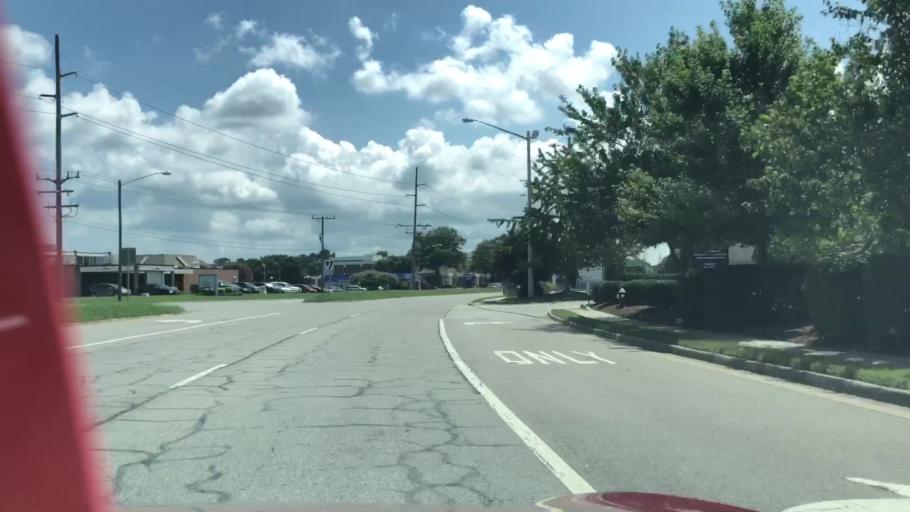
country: US
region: Virginia
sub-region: City of Virginia Beach
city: Virginia Beach
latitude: 36.8684
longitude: -76.0308
